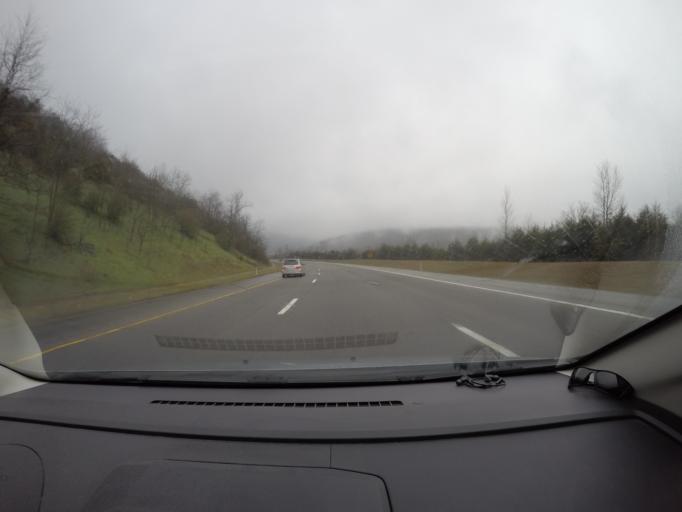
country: US
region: Tennessee
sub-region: Marion County
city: Monteagle
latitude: 35.1792
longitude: -85.8079
